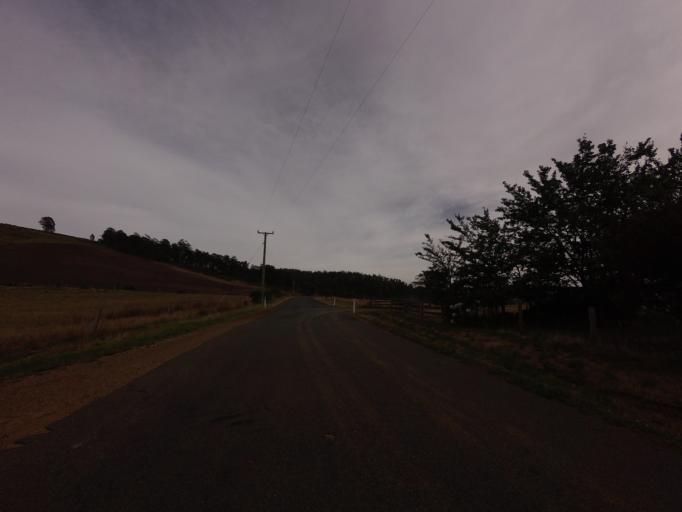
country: AU
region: Tasmania
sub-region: Sorell
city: Sorell
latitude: -42.4528
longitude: 147.5725
